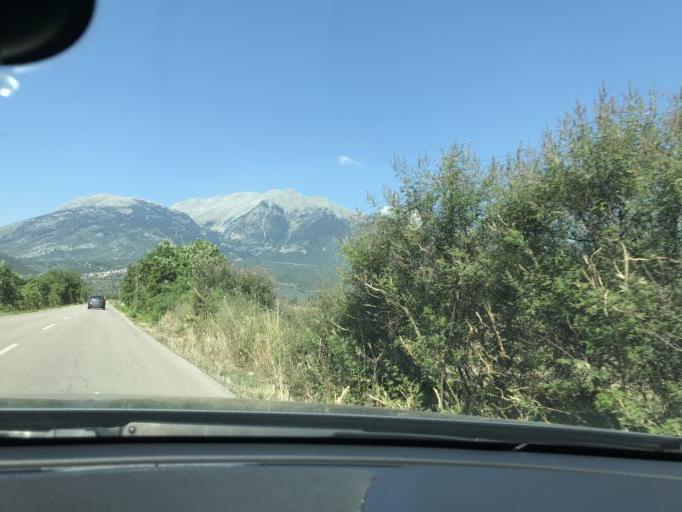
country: GR
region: Central Greece
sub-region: Nomos Fthiotidos
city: Kato Tithorea
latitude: 38.5209
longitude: 22.7716
